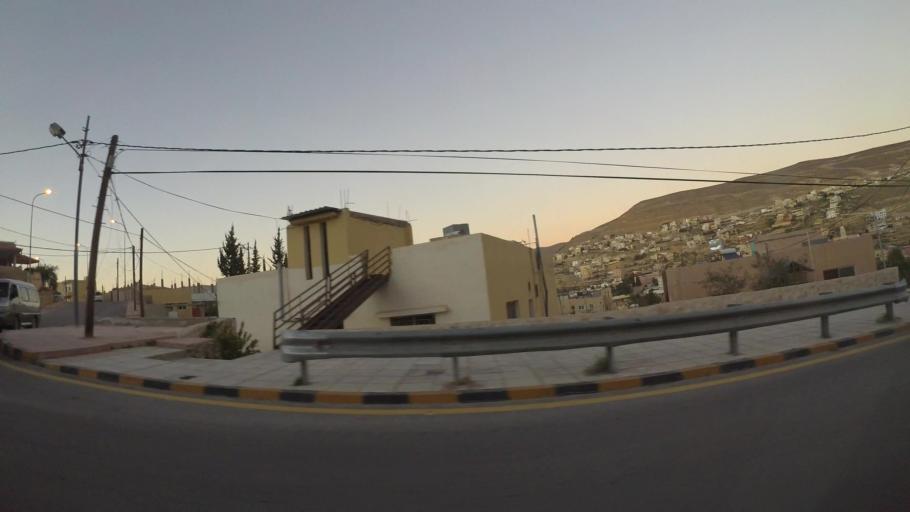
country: JO
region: Ma'an
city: Petra
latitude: 30.3162
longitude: 35.4757
